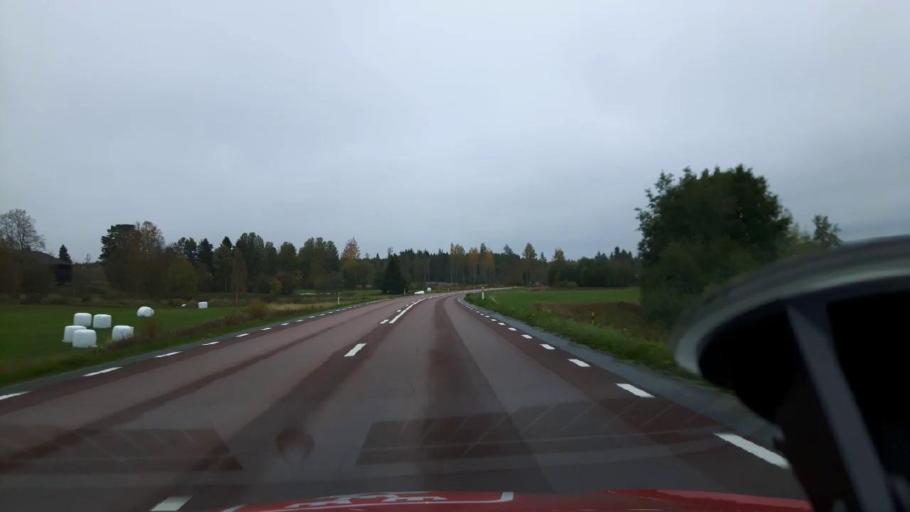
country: SE
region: Jaemtland
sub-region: Bergs Kommun
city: Hoverberg
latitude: 62.7606
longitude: 14.4377
